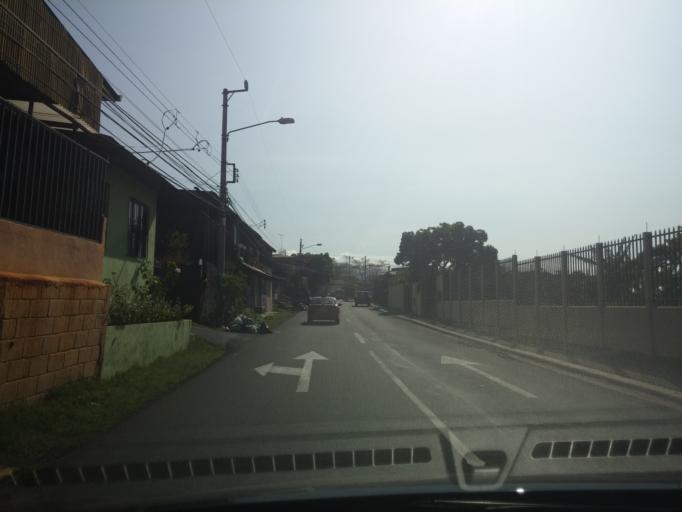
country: CR
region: Heredia
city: Llorente
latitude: 9.9997
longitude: -84.1515
